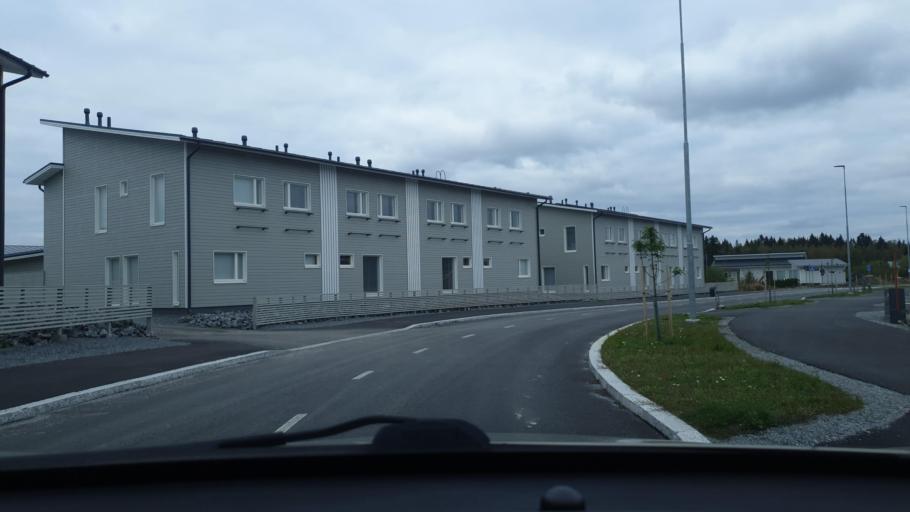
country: FI
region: Ostrobothnia
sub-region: Vaasa
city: Korsholm
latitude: 63.1293
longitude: 21.6509
